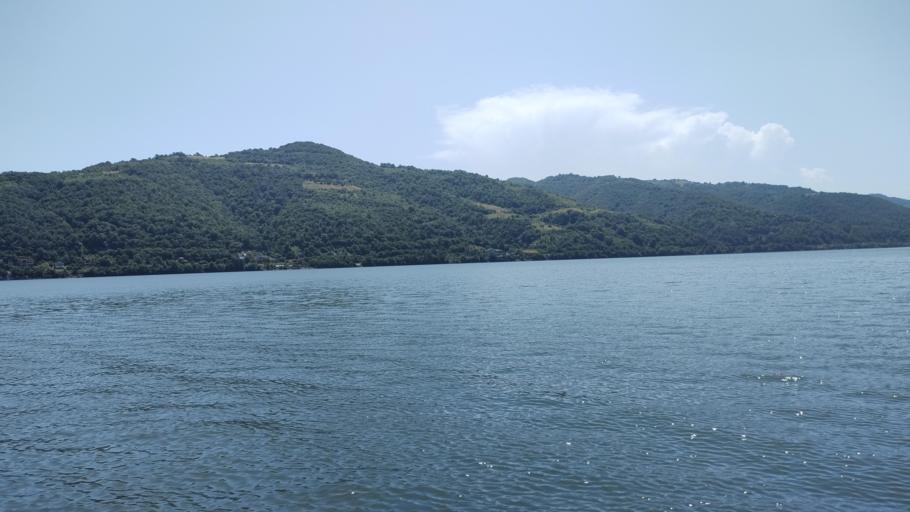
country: RO
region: Mehedinti
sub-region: Comuna Dubova
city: Dubova
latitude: 44.5307
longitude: 22.2078
